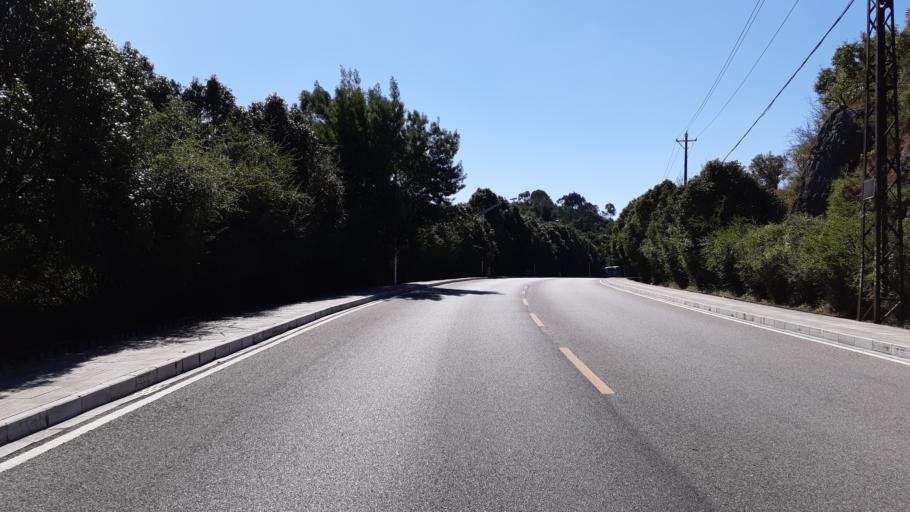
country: CN
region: Yunnan
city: Shilin
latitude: 24.8346
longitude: 103.3268
